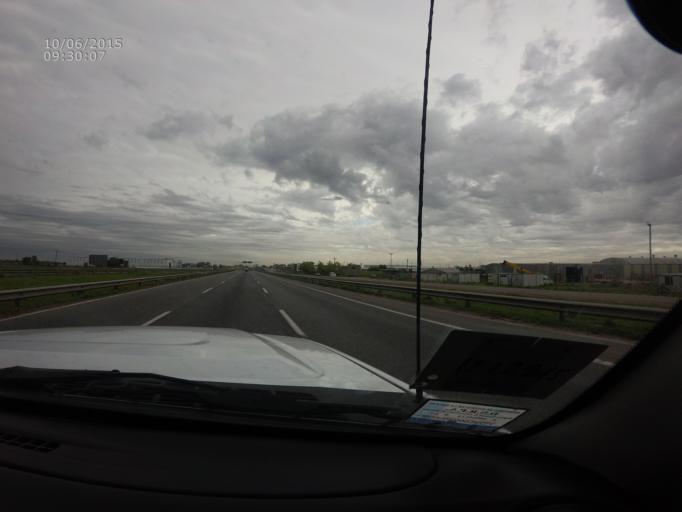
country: AR
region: Buenos Aires
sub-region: Partido de Zarate
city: Zarate
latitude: -34.1437
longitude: -59.0396
